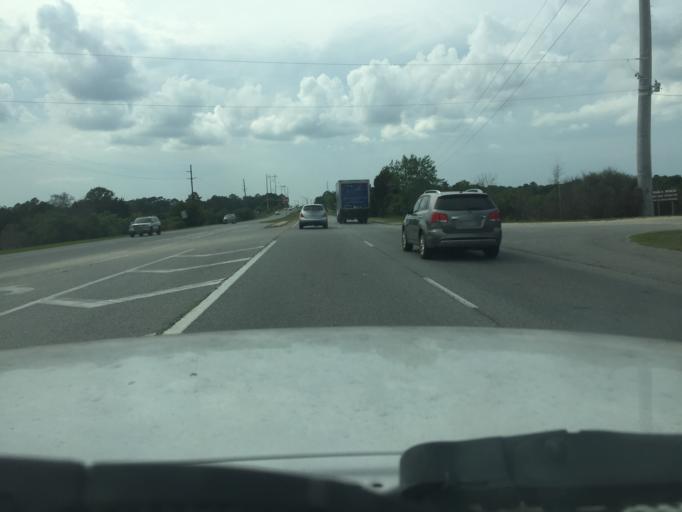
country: US
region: Georgia
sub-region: Chatham County
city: Whitemarsh Island
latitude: 32.0590
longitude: -81.0232
